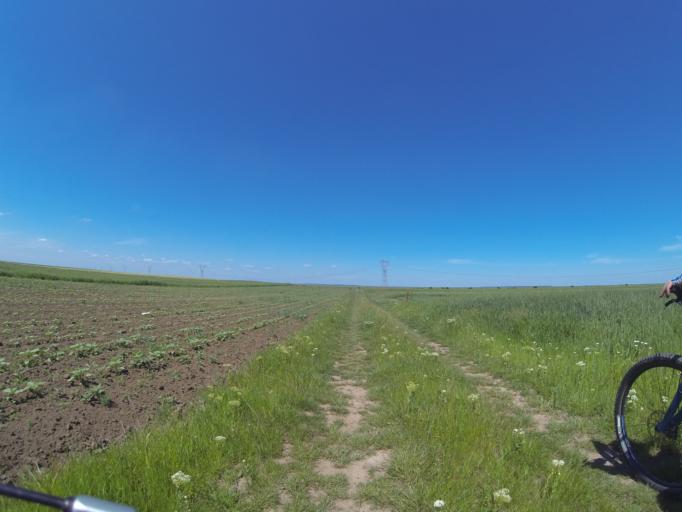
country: RO
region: Dolj
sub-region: Comuna Leu
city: Leu
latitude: 44.2082
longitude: 24.0358
